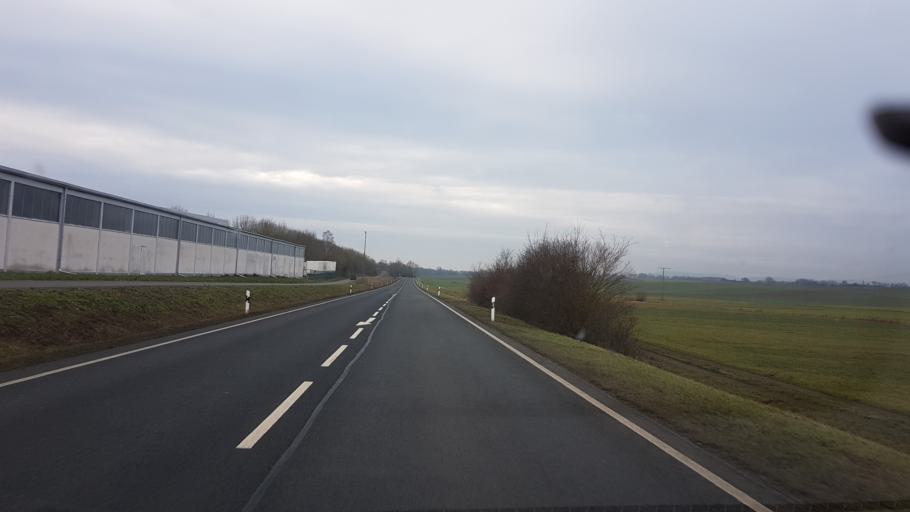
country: DE
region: Bavaria
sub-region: Regierungsbezirk Unterfranken
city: Ermershausen
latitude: 50.2375
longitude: 10.5688
